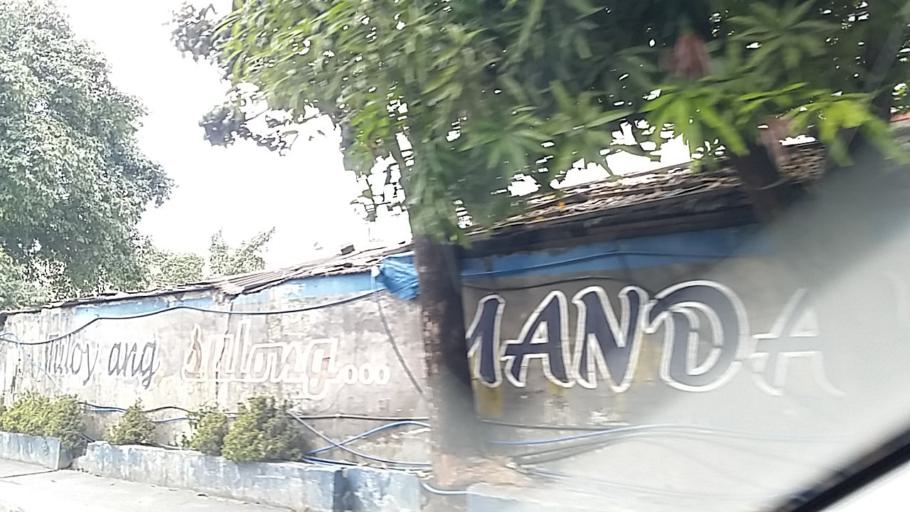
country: PH
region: Metro Manila
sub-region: Mandaluyong
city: Mandaluyong City
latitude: 14.5824
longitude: 121.0445
